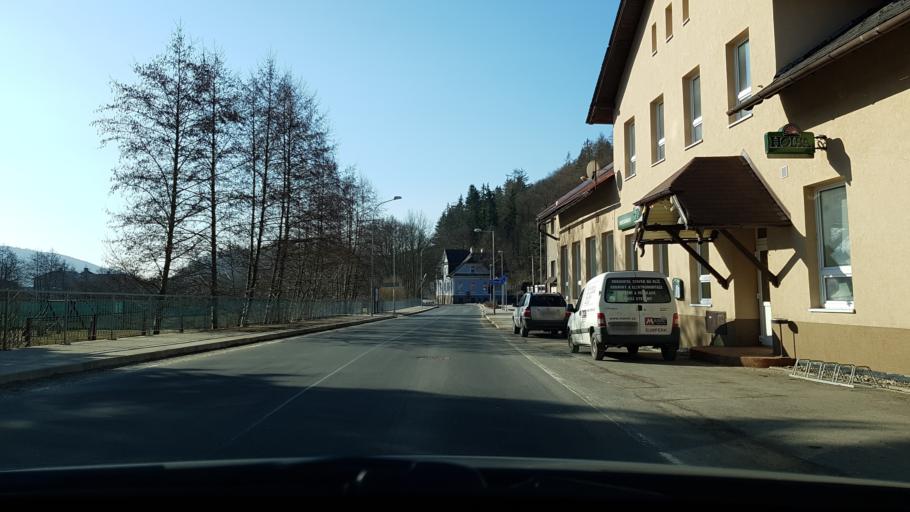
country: CZ
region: Olomoucky
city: Dolni Bohdikov
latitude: 50.0279
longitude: 16.8993
